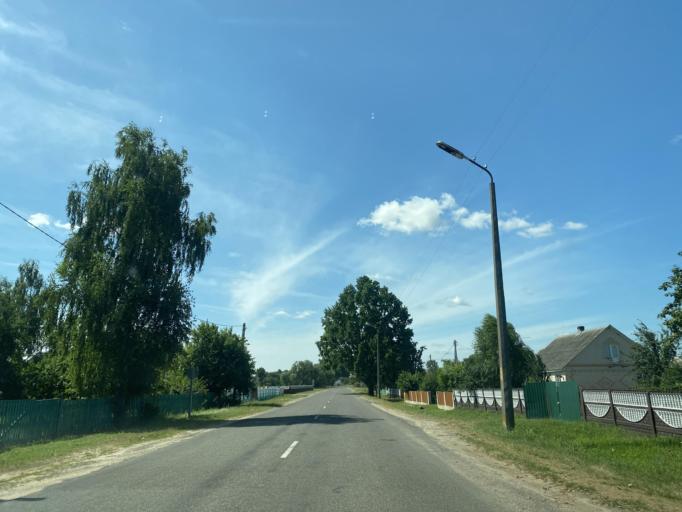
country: BY
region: Brest
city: Ivanava
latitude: 52.1852
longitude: 25.6084
